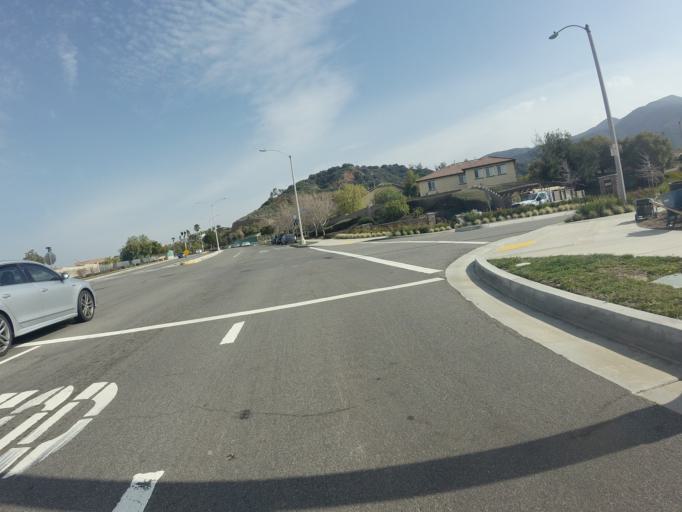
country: US
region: California
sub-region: Riverside County
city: Corona
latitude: 33.8425
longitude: -117.5994
